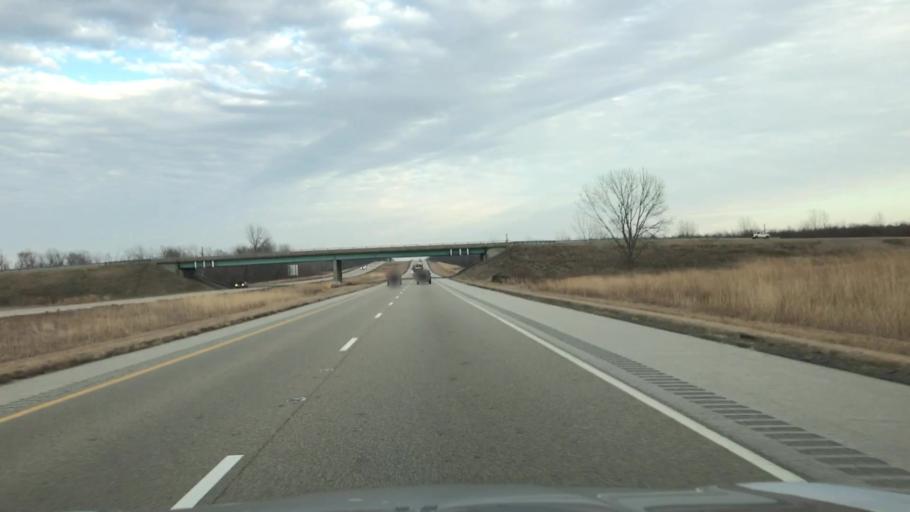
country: US
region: Illinois
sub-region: Logan County
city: Lincoln
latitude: 40.1813
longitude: -89.3894
